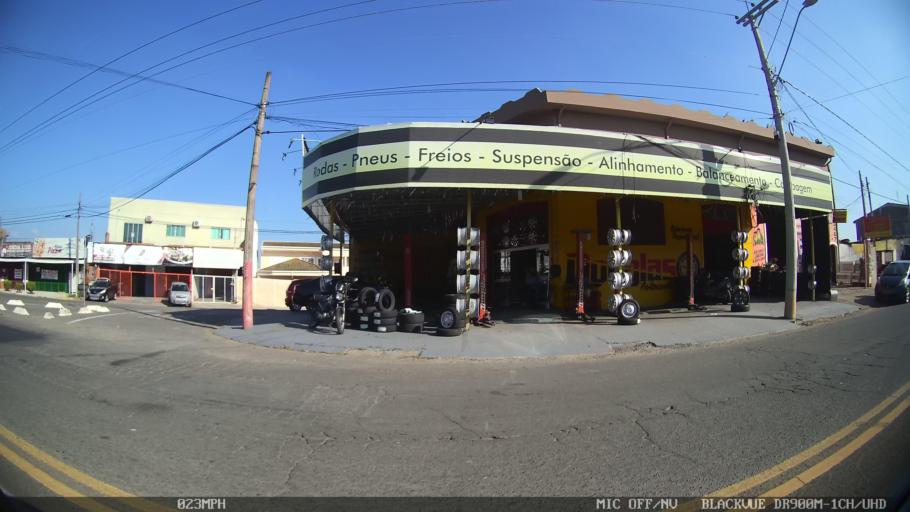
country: BR
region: Sao Paulo
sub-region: Campinas
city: Campinas
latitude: -22.9889
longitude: -47.1441
